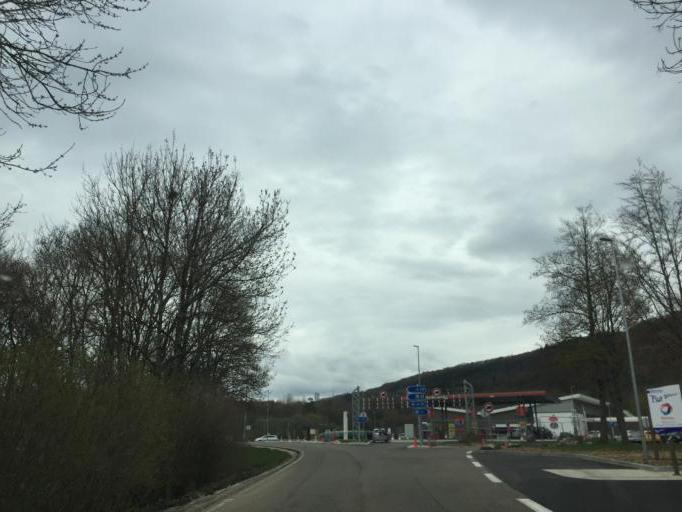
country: FR
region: Rhone-Alpes
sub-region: Departement de l'Ain
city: Saint-Martin-du-Frene
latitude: 46.1149
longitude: 5.4920
